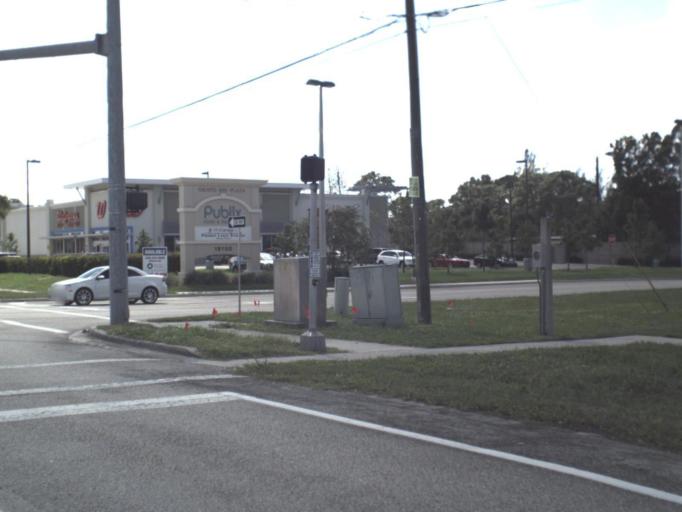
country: US
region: Florida
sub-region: Lee County
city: San Carlos Park
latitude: 26.4634
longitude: -81.8306
